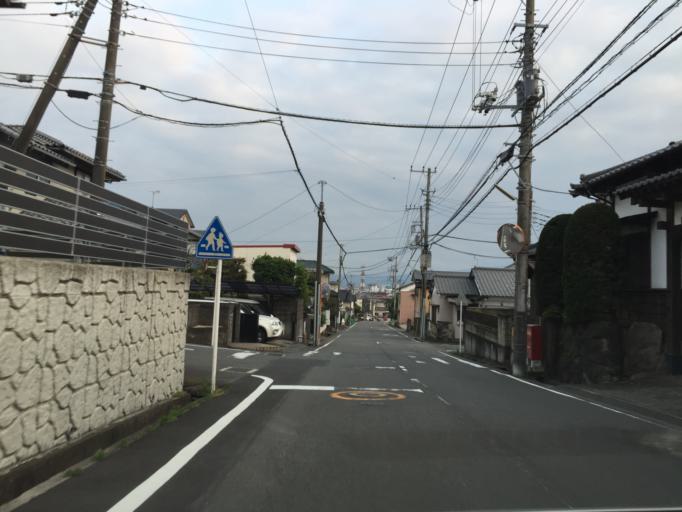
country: JP
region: Shizuoka
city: Numazu
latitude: 35.1276
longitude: 138.8586
